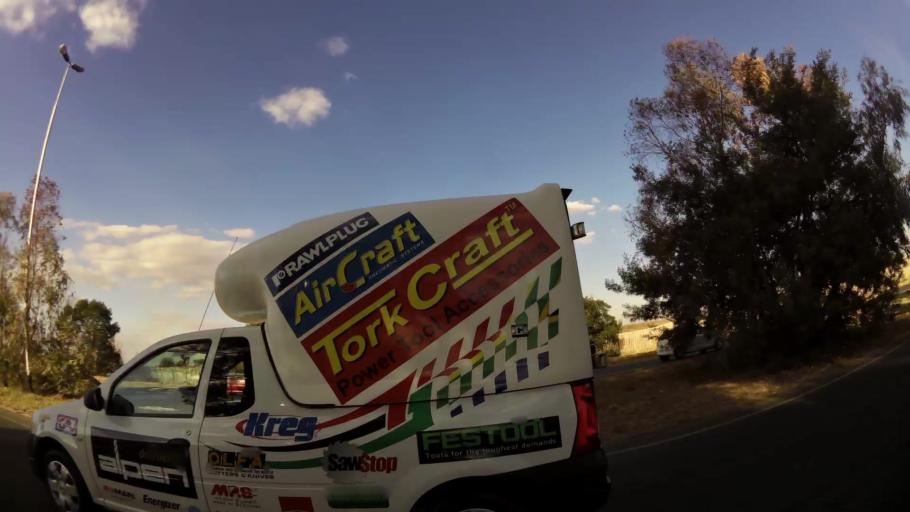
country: ZA
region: Gauteng
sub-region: City of Johannesburg Metropolitan Municipality
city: Midrand
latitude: -25.9784
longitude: 28.1340
